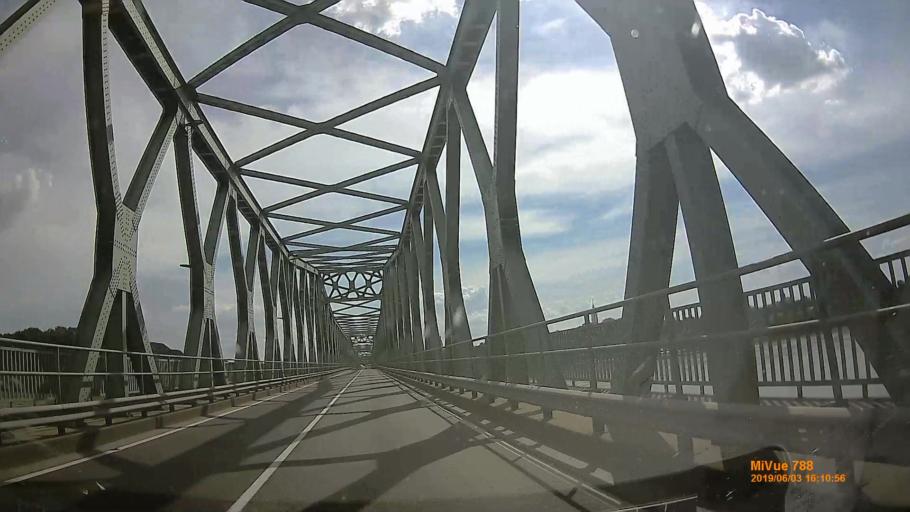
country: HU
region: Tolna
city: Dunafoldvar
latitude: 46.8114
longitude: 18.9339
